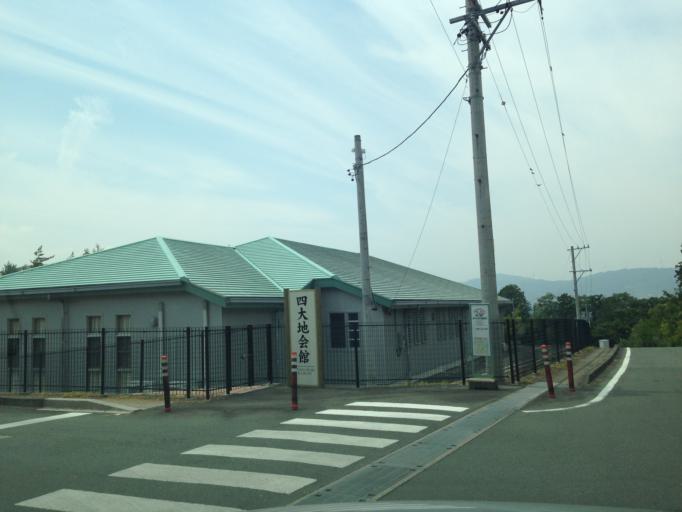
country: JP
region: Shizuoka
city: Hamakita
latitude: 34.8434
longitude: 137.7676
